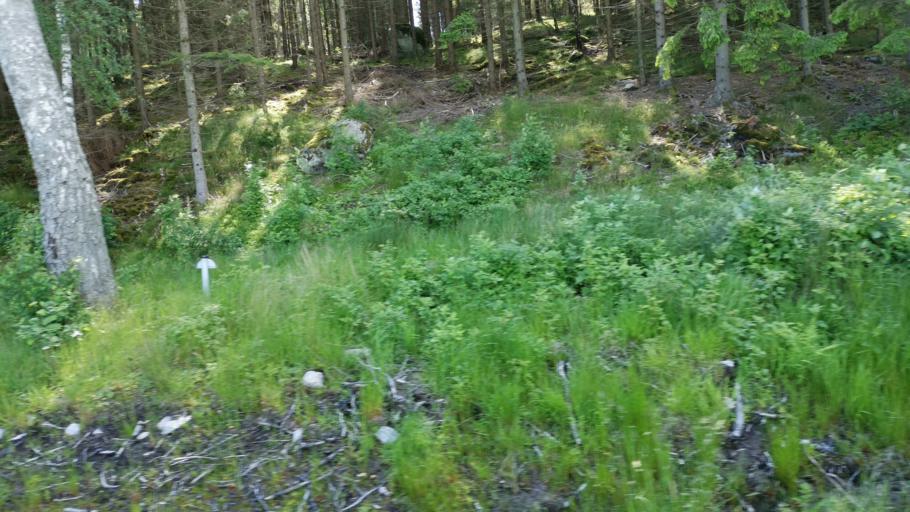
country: SE
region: Vaestra Goetaland
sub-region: Orust
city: Henan
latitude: 58.3200
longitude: 11.7189
